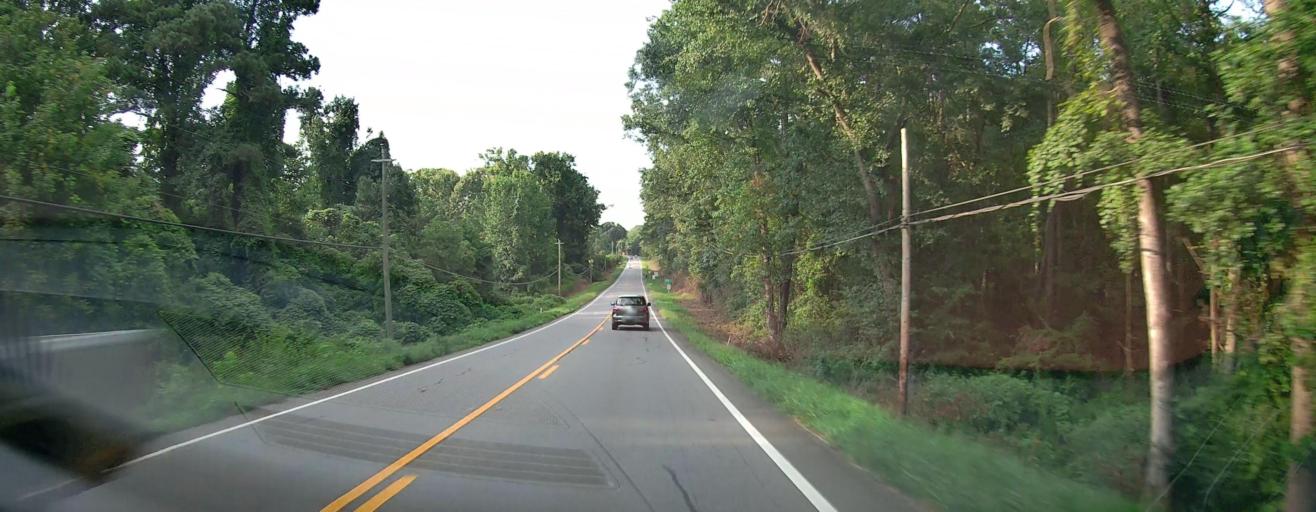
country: US
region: Georgia
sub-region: Monroe County
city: Forsyth
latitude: 33.0193
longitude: -83.9403
